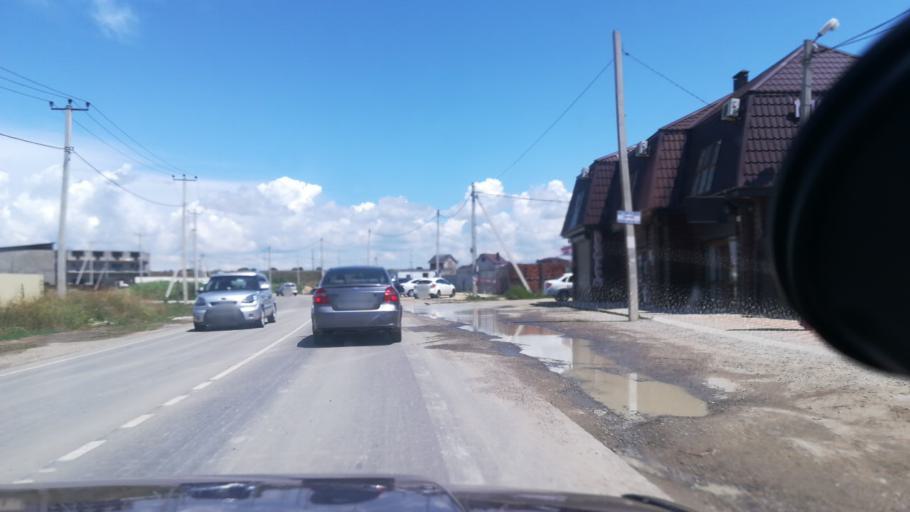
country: RU
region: Krasnodarskiy
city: Vityazevo
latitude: 44.9649
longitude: 37.2926
